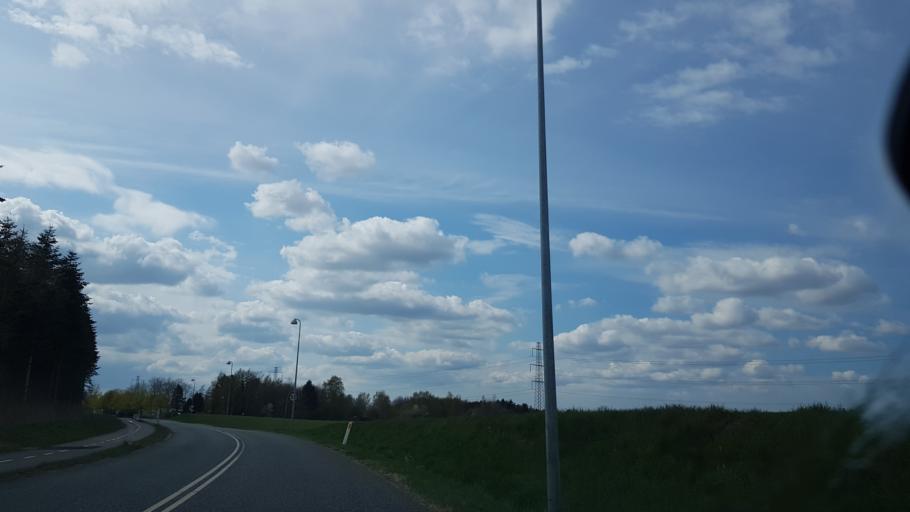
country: DK
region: Capital Region
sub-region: Allerod Kommune
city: Lillerod
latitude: 55.8921
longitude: 12.3548
